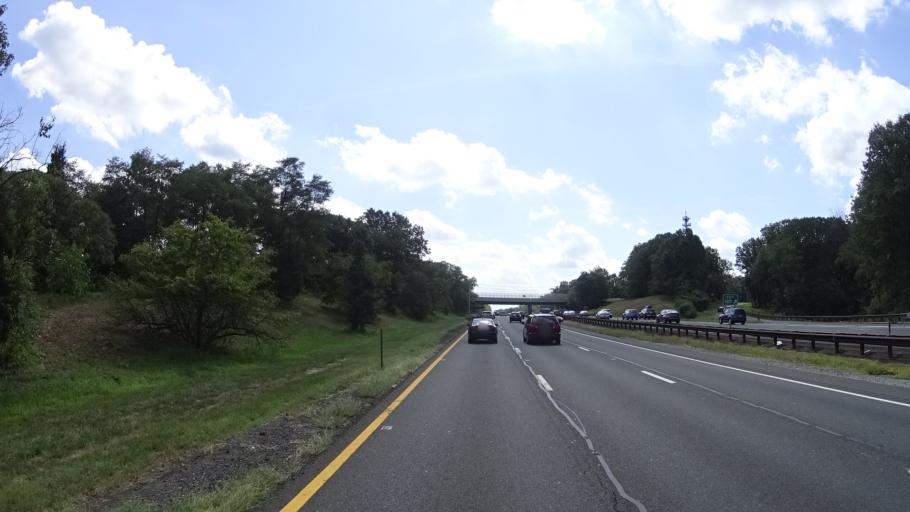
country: US
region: New Jersey
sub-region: Middlesex County
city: Laurence Harbor
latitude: 40.4357
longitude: -74.2533
